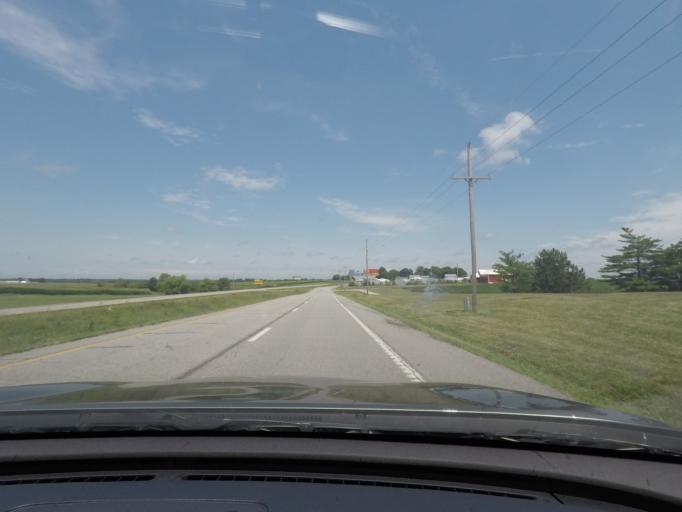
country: US
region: Missouri
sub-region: Saline County
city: Marshall
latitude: 39.0630
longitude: -93.1957
